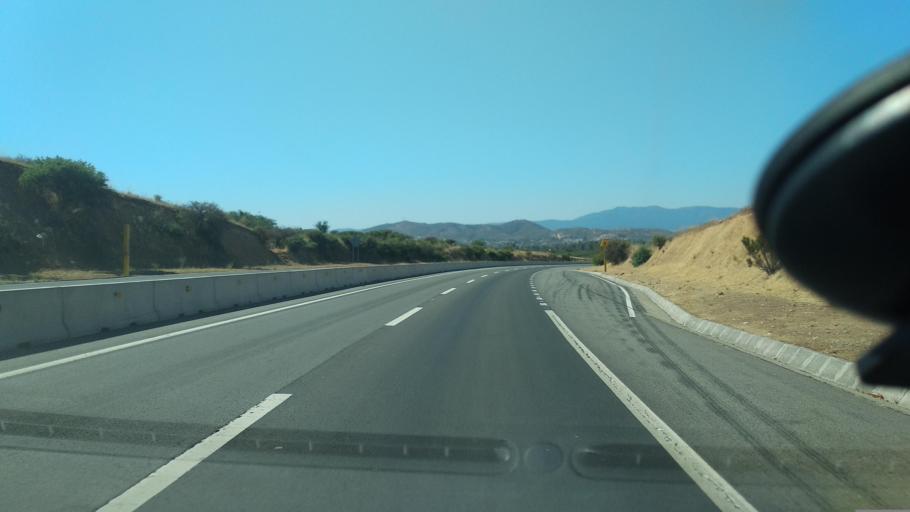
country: CL
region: Valparaiso
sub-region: Provincia de Marga Marga
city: Villa Alemana
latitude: -32.9977
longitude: -71.3298
